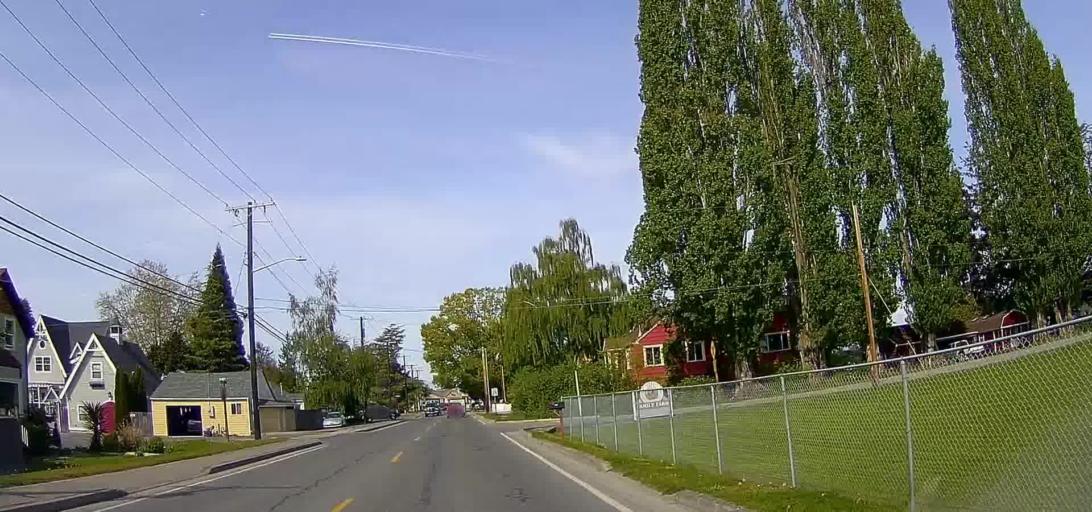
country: US
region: Washington
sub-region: Skagit County
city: Mount Vernon
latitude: 48.3900
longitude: -122.4908
